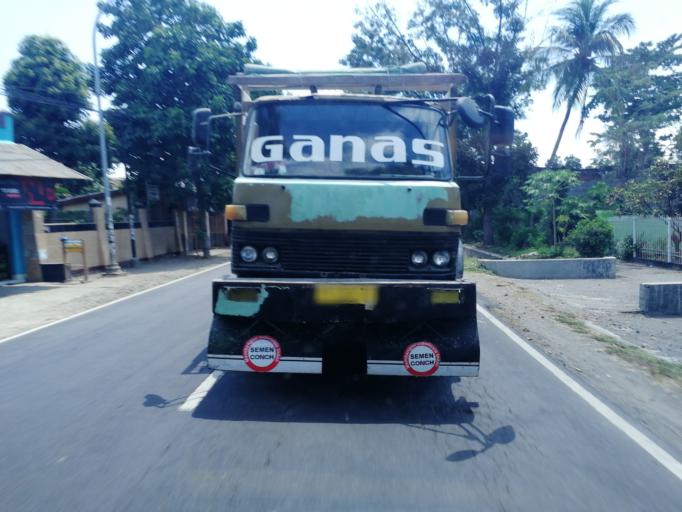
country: ID
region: West Nusa Tenggara
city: Jelateng Timur
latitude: -8.7039
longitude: 116.0914
